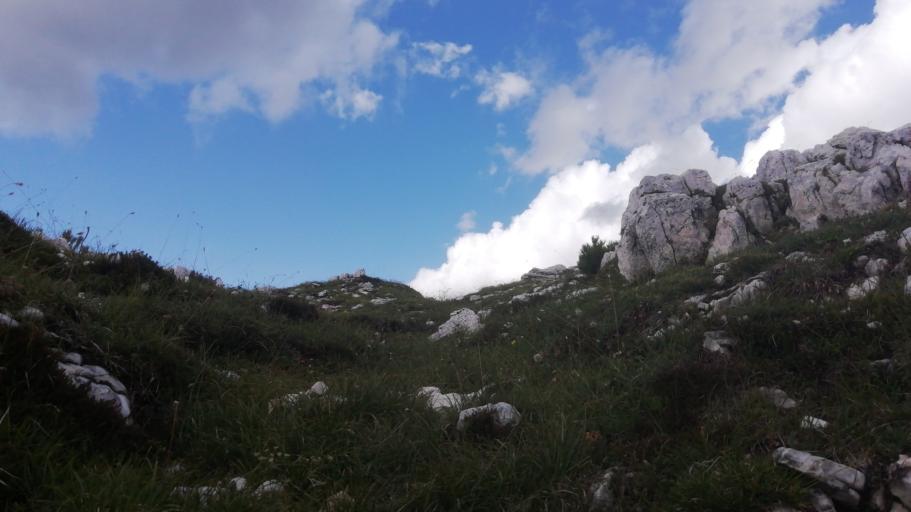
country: IT
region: Trentino-Alto Adige
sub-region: Bolzano
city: Dobbiaco
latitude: 46.6206
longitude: 12.2477
